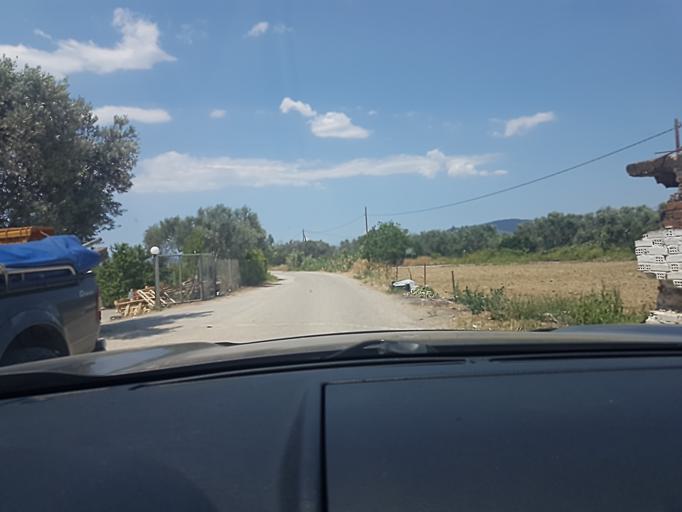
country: GR
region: Central Greece
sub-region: Nomos Evvoias
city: Ayios Nikolaos
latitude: 38.4159
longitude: 23.6606
